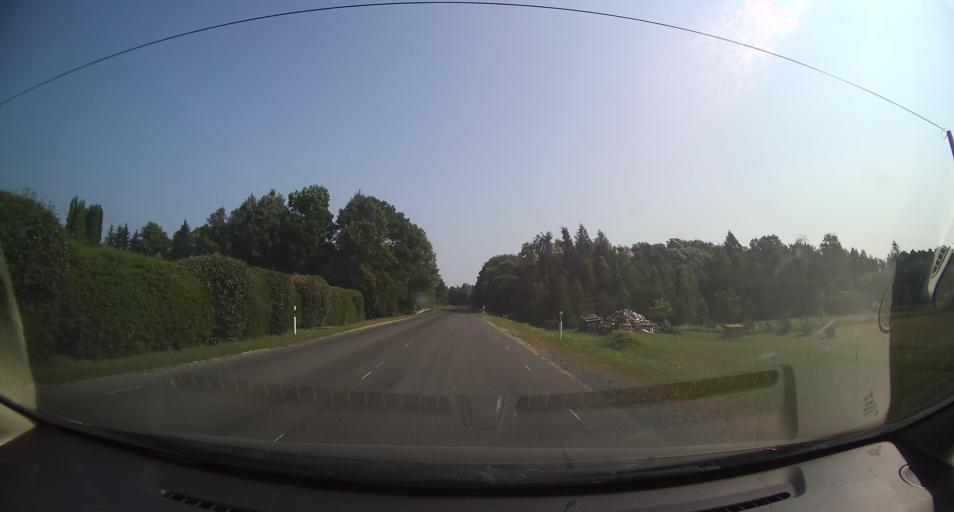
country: EE
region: Paernumaa
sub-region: Audru vald
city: Audru
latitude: 58.4698
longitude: 24.3198
